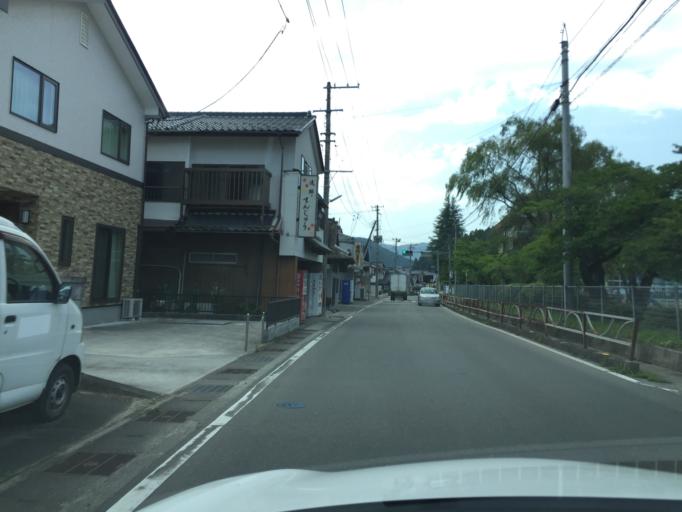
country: JP
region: Fukushima
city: Iwaki
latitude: 37.0359
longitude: 140.7080
